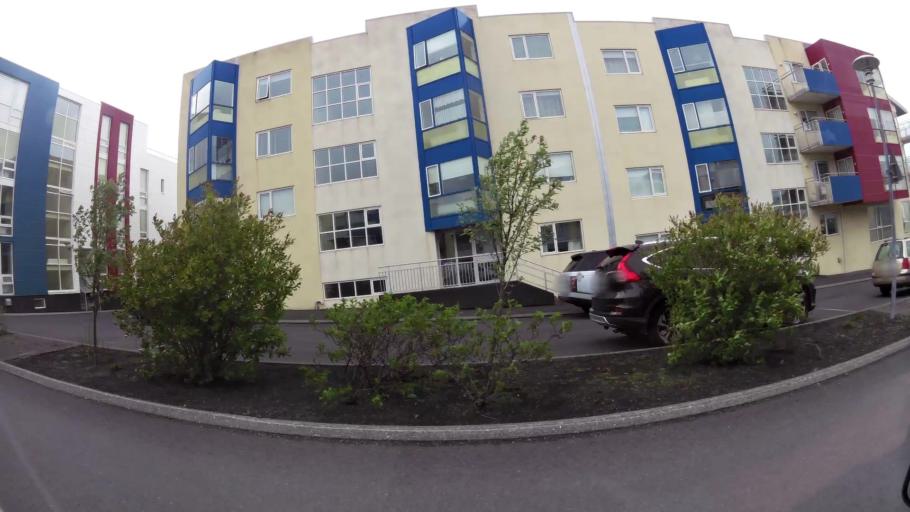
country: IS
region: Capital Region
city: Gardabaer
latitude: 64.0926
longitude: -21.9442
